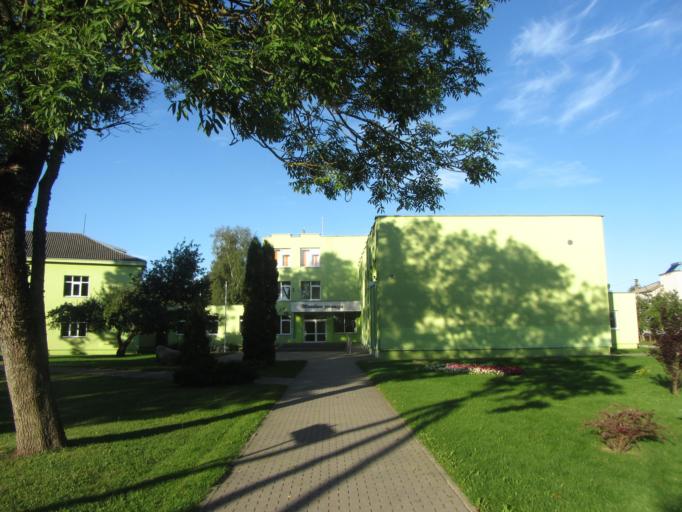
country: LT
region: Alytaus apskritis
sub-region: Alytus
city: Alytus
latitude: 54.3298
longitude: 23.8989
